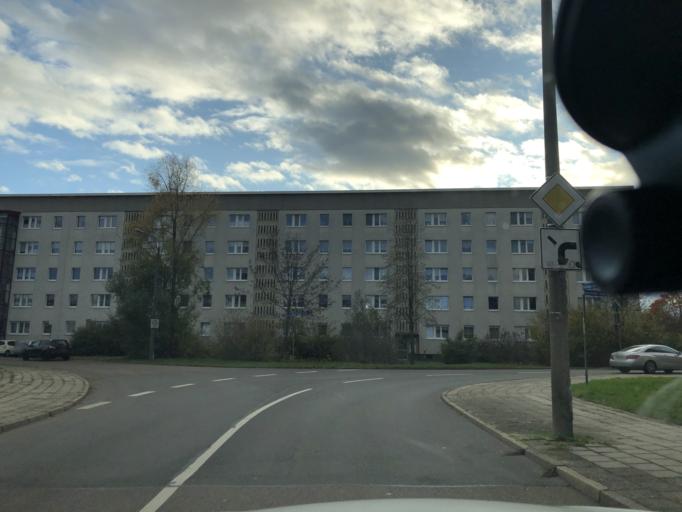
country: DE
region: Saxony-Anhalt
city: Halle Neustadt
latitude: 51.4729
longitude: 11.9106
